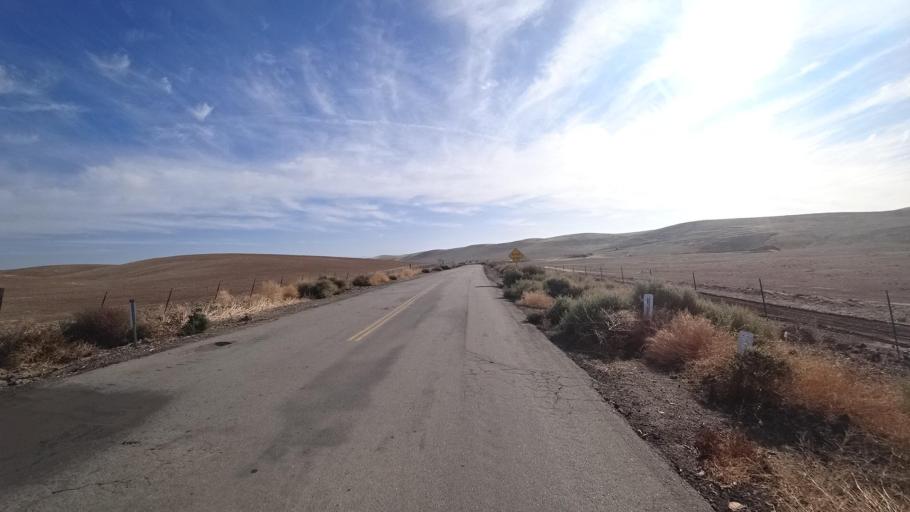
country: US
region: California
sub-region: Tulare County
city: Richgrove
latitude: 35.6211
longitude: -119.0275
